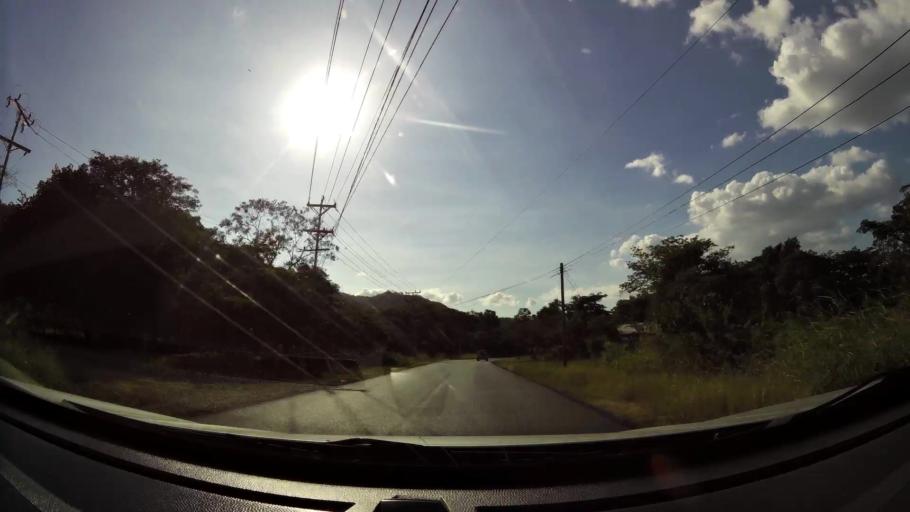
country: CR
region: Guanacaste
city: Sardinal
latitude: 10.5357
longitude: -85.6810
